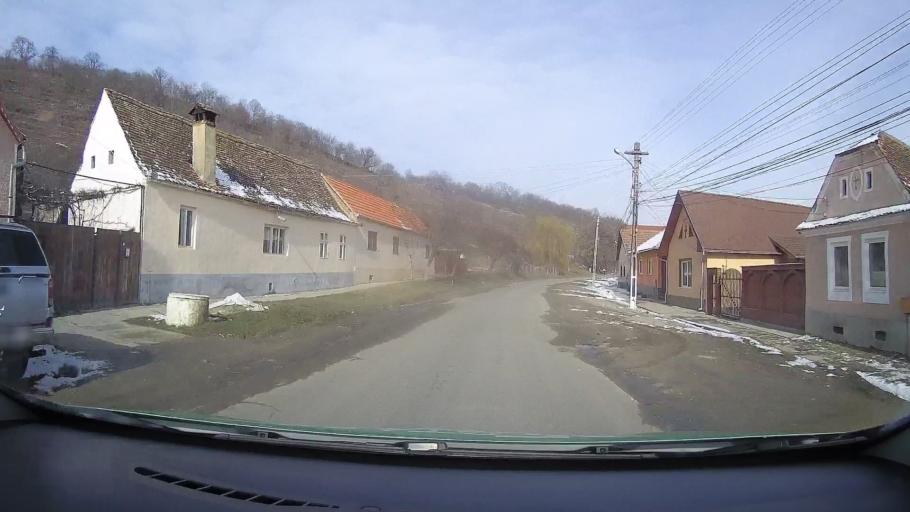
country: RO
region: Sibiu
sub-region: Comuna Laslea
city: Laslea
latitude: 46.2111
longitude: 24.6578
